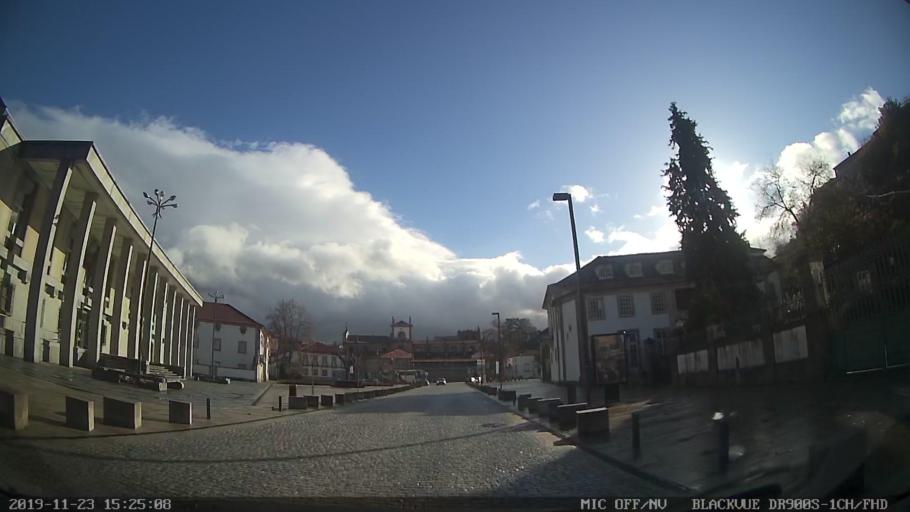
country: PT
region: Viseu
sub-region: Lamego
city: Lamego
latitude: 41.0986
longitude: -7.8070
